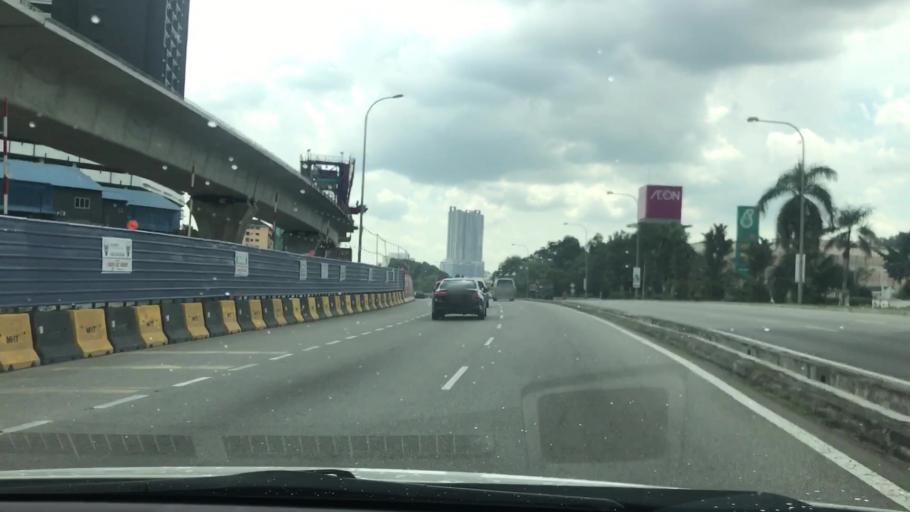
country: MY
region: Putrajaya
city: Putrajaya
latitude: 2.9946
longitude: 101.6768
